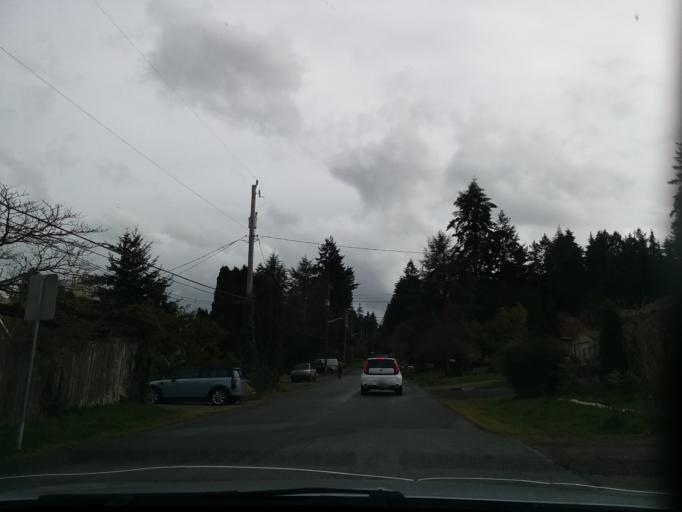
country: US
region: Washington
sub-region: Snohomish County
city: Mountlake Terrace
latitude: 47.7682
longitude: -122.3125
